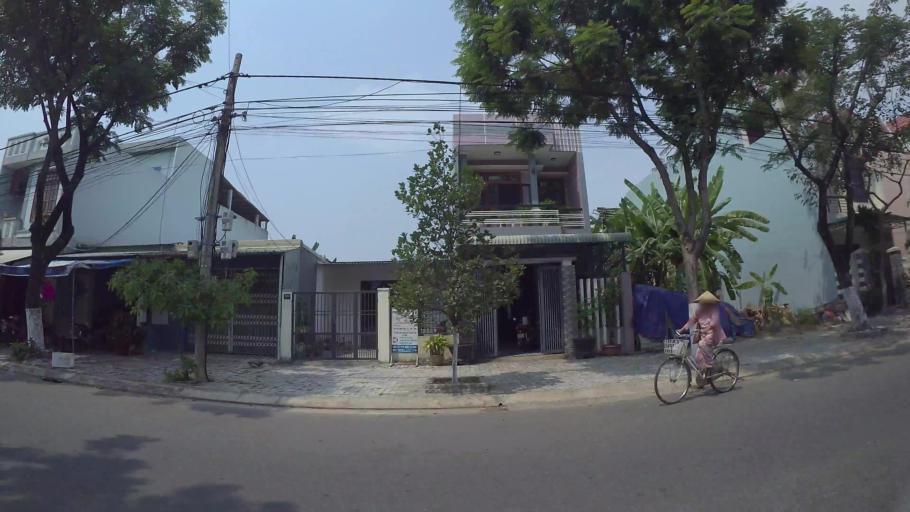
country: VN
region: Da Nang
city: Cam Le
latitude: 15.9992
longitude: 108.2105
